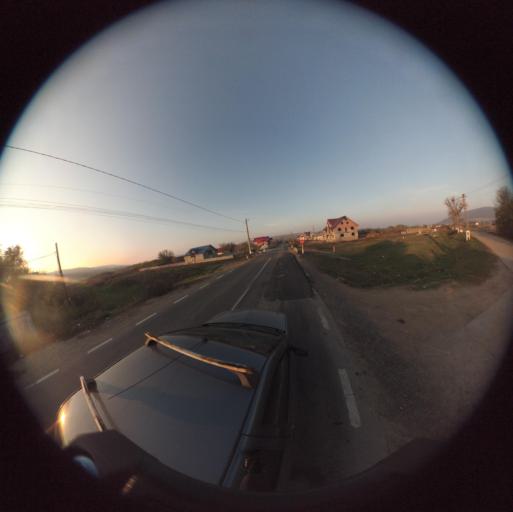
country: RO
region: Vaslui
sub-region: Comuna Bacesti
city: Bacesti
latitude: 46.8271
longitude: 27.2507
